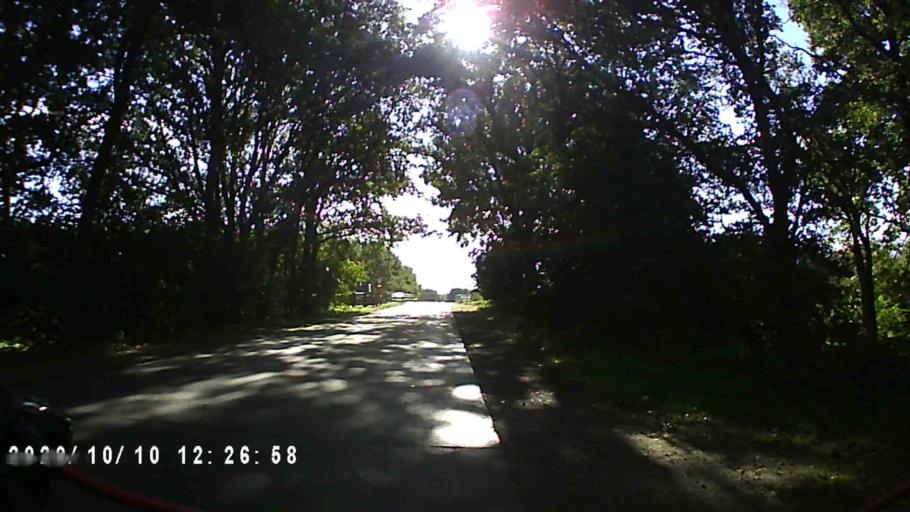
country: NL
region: Friesland
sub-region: Gemeente Heerenveen
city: Jubbega
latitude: 52.9832
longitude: 6.1809
